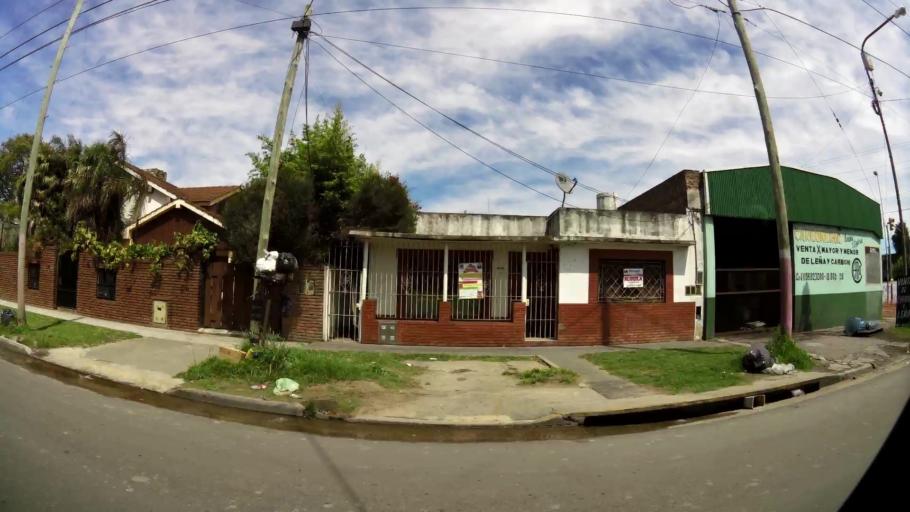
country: AR
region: Buenos Aires
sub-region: Partido de Quilmes
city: Quilmes
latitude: -34.7572
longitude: -58.2981
